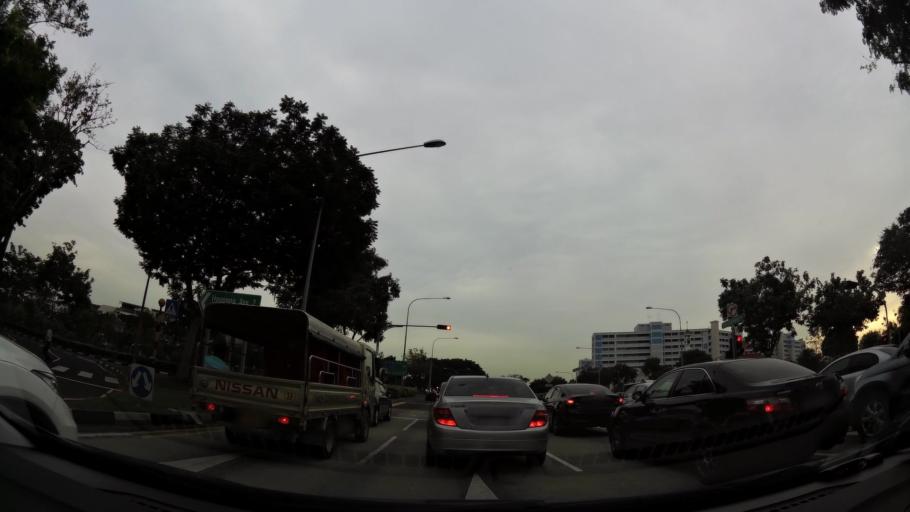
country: SG
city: Singapore
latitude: 1.3703
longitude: 103.8766
